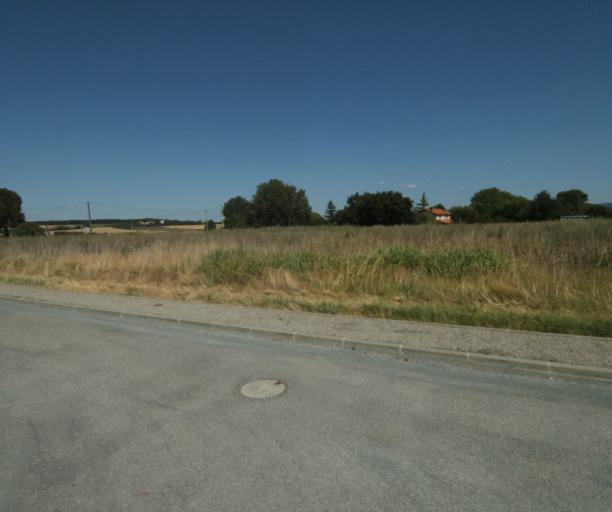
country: FR
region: Midi-Pyrenees
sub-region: Departement de la Haute-Garonne
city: Saint-Felix-Lauragais
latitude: 43.4886
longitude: 1.9044
